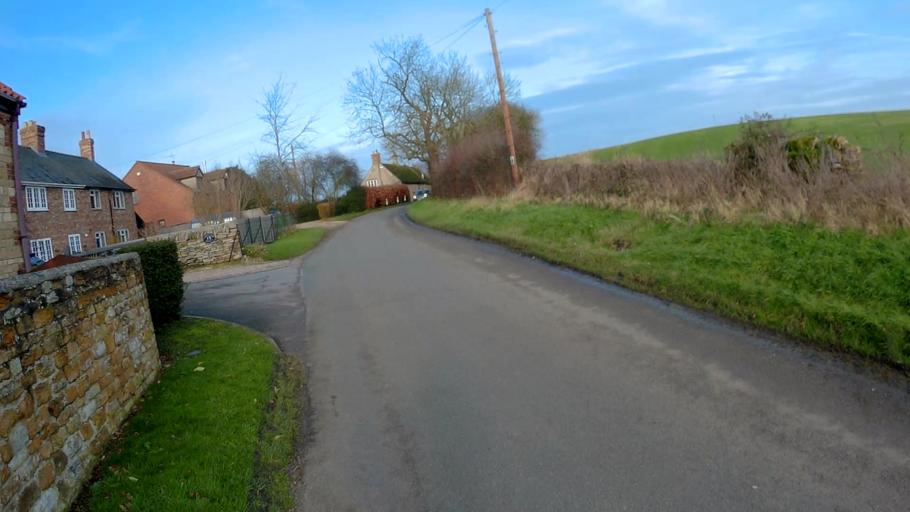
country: GB
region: England
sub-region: Lincolnshire
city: Bourne
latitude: 52.7508
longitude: -0.4166
